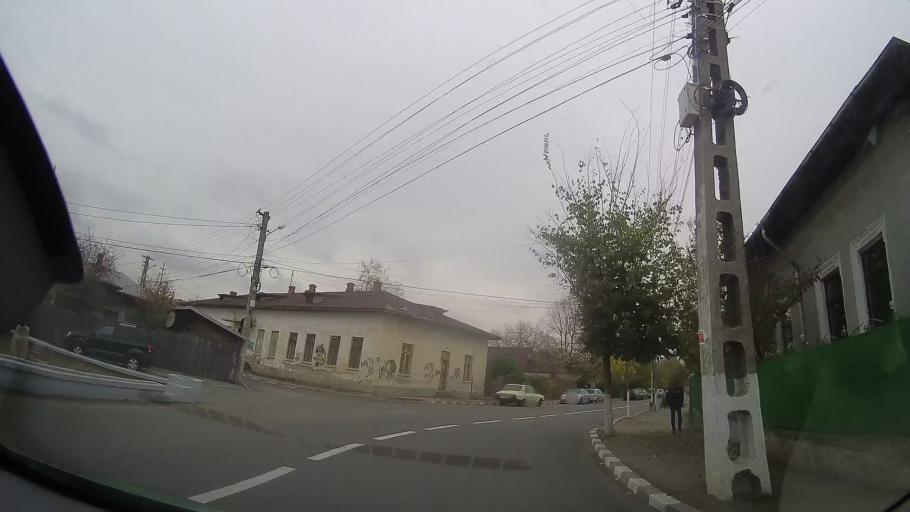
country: RO
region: Prahova
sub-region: Oras Urlati
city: Urlati
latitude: 44.9928
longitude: 26.2311
